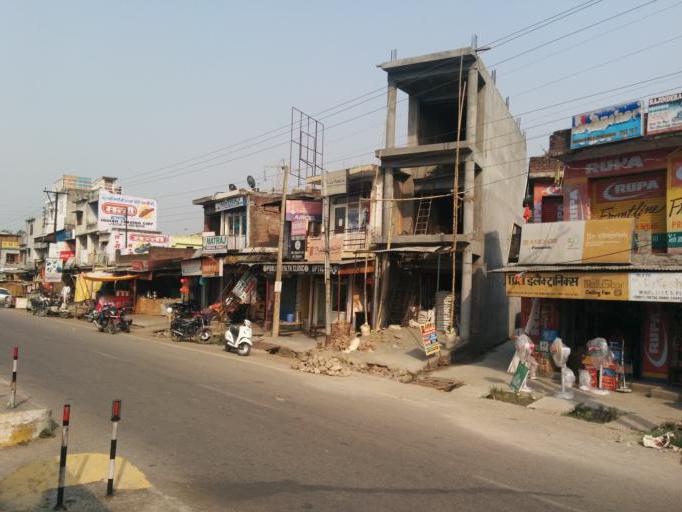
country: IN
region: Punjab
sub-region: Gurdaspur
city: Dharkalan
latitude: 32.2811
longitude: 75.8476
